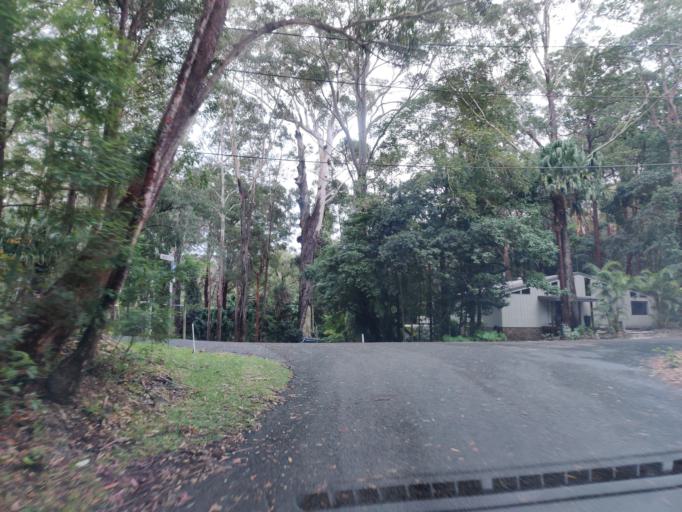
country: AU
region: New South Wales
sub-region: Great Lakes
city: Forster
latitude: -32.3861
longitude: 152.5027
